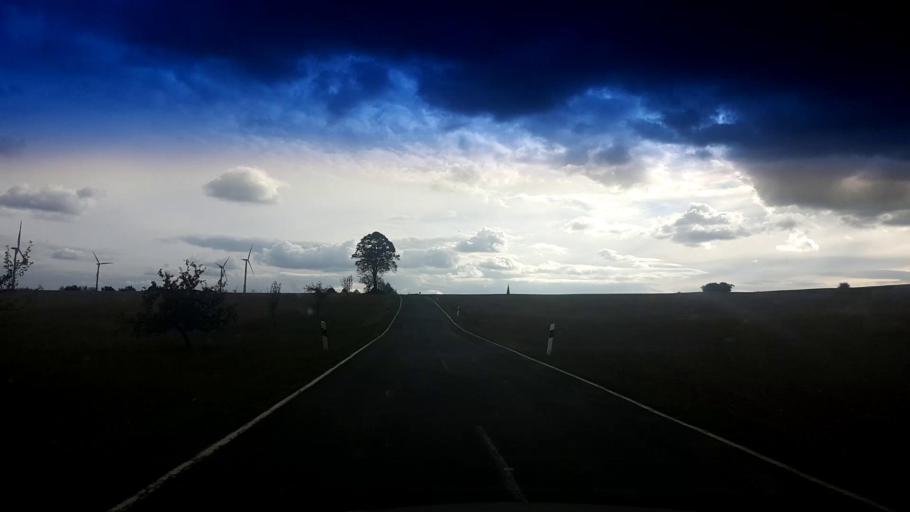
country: DE
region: Bavaria
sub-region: Upper Franconia
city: Poxdorf
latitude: 49.9590
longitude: 11.0924
